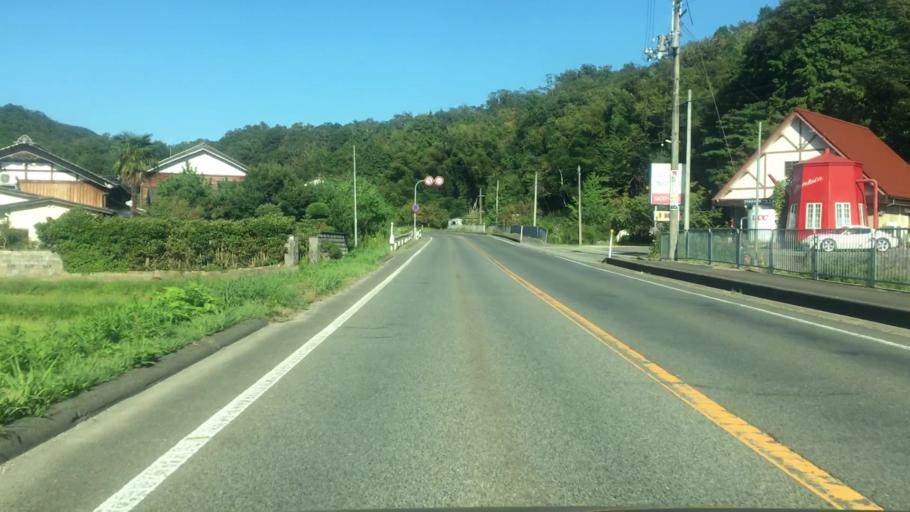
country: JP
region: Hyogo
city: Toyooka
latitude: 35.5577
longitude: 134.8484
